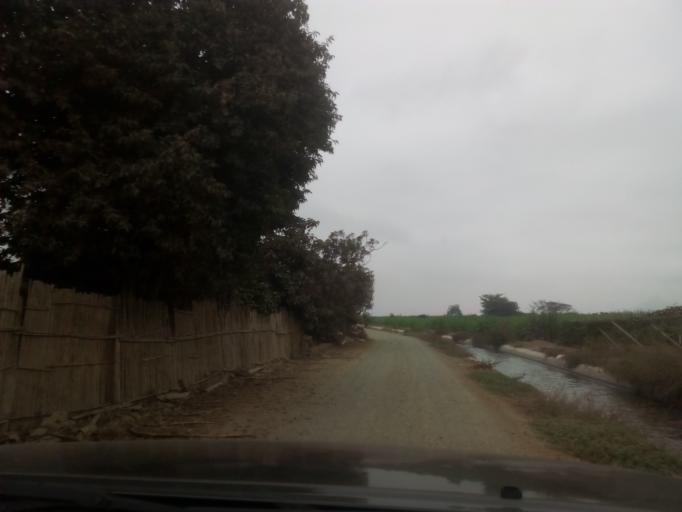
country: PE
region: La Libertad
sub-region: Viru
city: Viru
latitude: -8.4210
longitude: -78.8114
